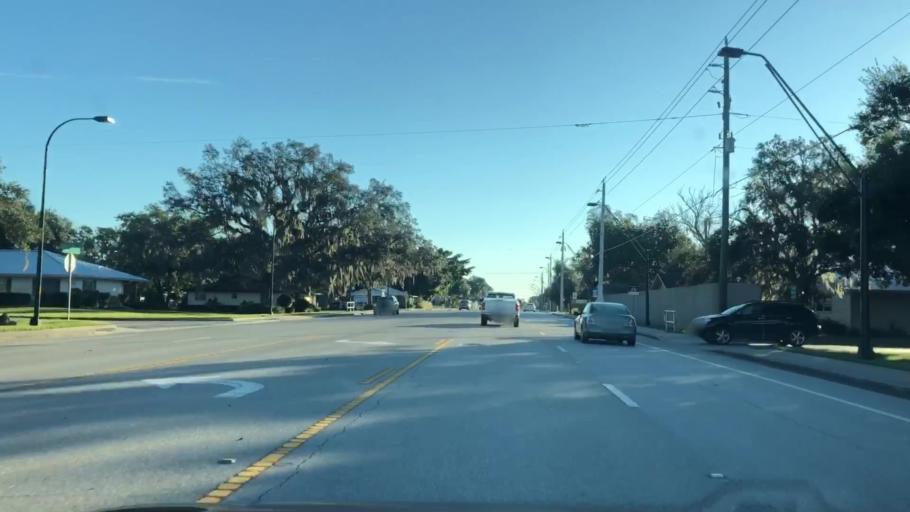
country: US
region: Florida
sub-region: Sarasota County
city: Fruitville
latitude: 27.3231
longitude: -82.4569
